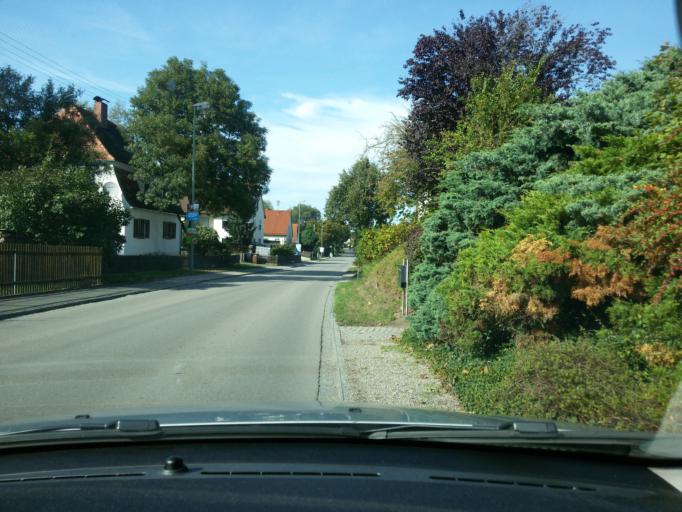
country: DE
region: Bavaria
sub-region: Swabia
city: Ustersbach
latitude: 48.3258
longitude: 10.6522
